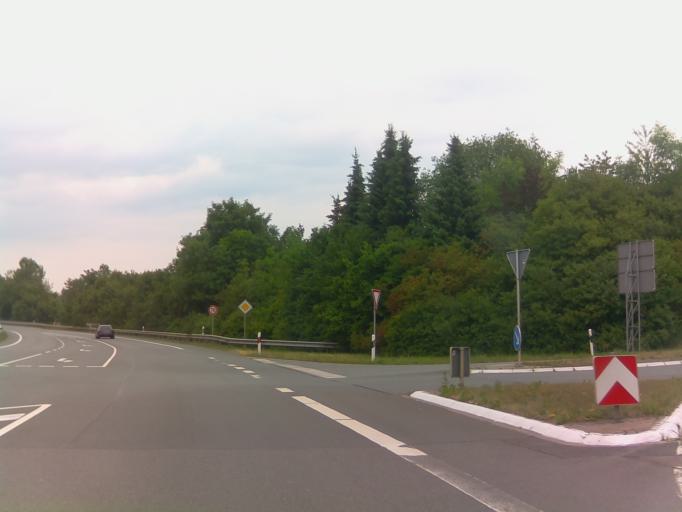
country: DE
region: North Rhine-Westphalia
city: Brakel
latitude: 51.6995
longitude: 9.1705
